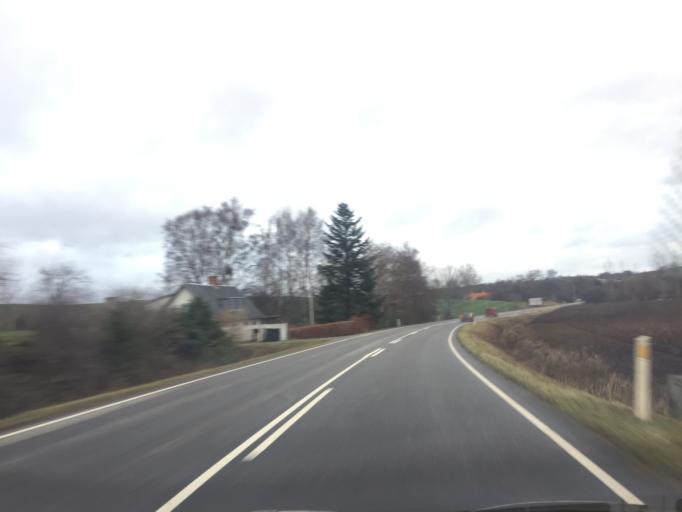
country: DK
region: Zealand
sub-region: Holbaek Kommune
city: Tollose
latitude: 55.6317
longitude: 11.7888
